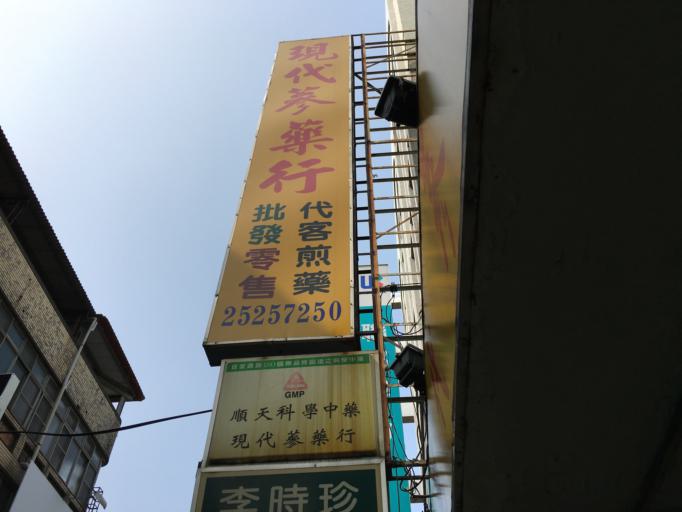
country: TW
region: Taiwan
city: Fengyuan
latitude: 24.2496
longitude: 120.7181
